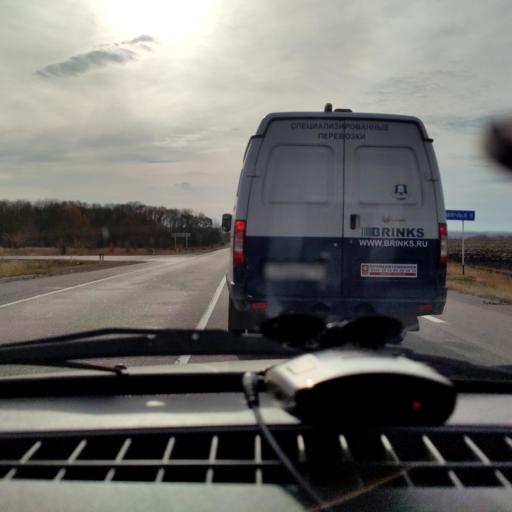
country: RU
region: Voronezj
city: Shilovo
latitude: 51.4587
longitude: 38.9712
